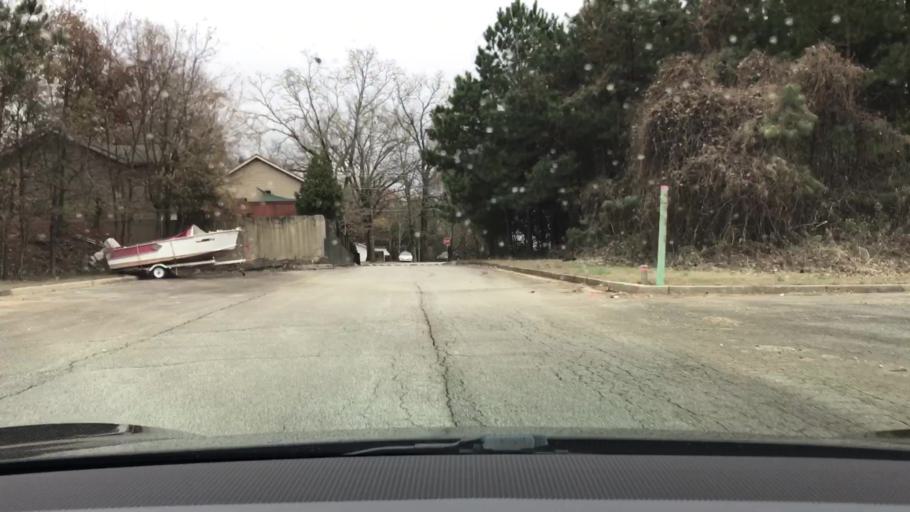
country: US
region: Georgia
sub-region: Gwinnett County
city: Buford
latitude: 34.1135
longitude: -84.0113
